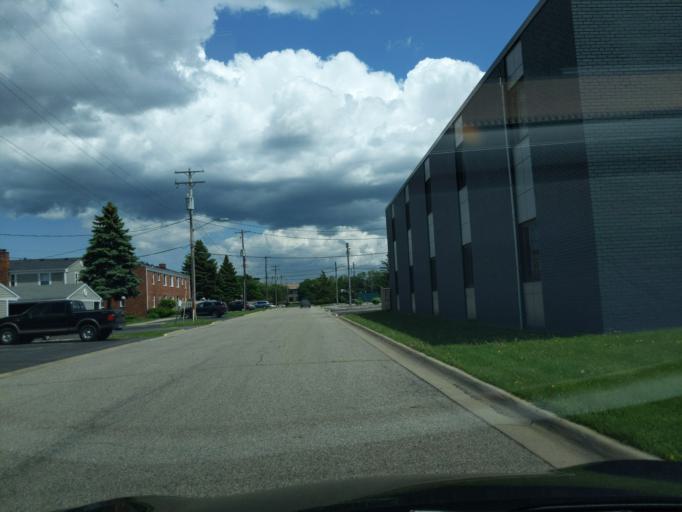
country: US
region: Michigan
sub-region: Ingham County
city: Lansing
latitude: 42.7441
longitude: -84.5211
